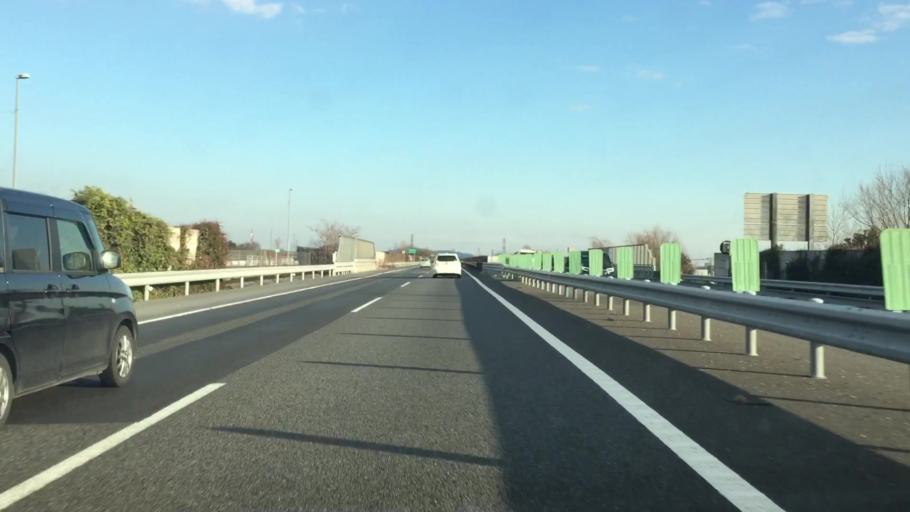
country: JP
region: Gunma
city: Isesaki
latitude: 36.3517
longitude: 139.2324
